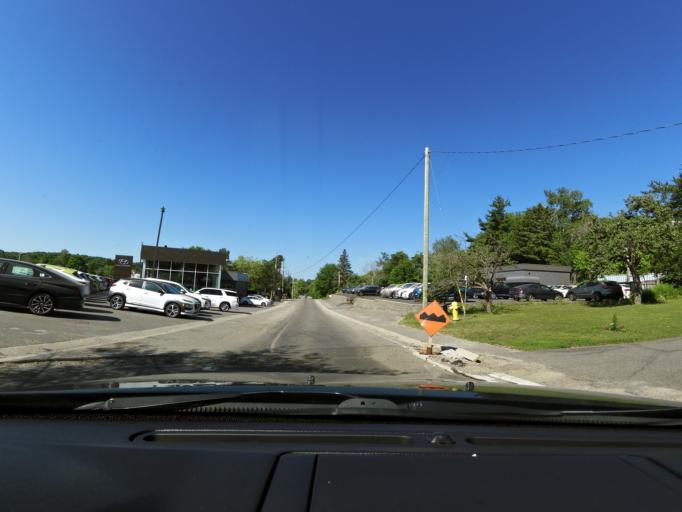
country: CA
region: Ontario
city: Huntsville
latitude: 45.3310
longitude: -79.2100
